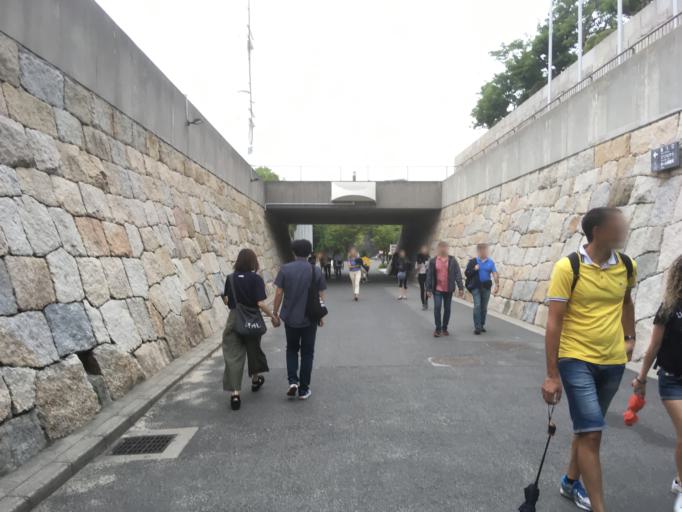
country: JP
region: Osaka
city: Osaka-shi
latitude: 34.6890
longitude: 135.5308
